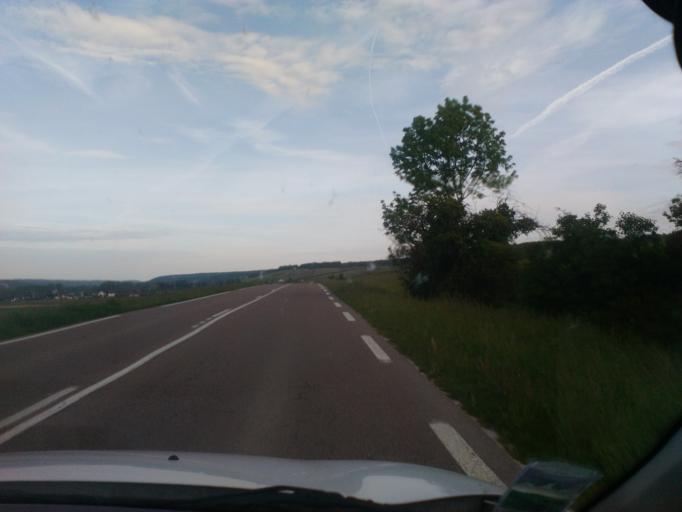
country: FR
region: Champagne-Ardenne
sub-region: Departement de l'Aube
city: Bar-sur-Aube
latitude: 48.2558
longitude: 4.6805
